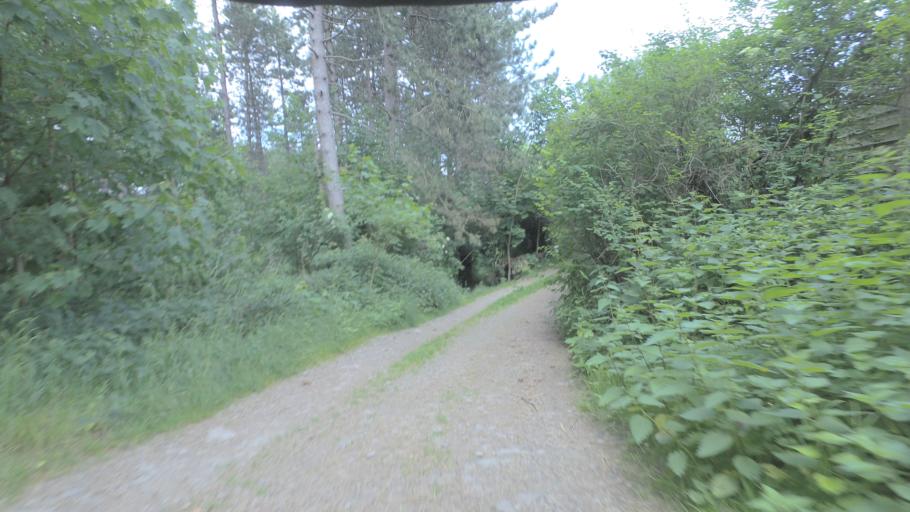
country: DE
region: Lower Saxony
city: Goslar
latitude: 51.8973
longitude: 10.4701
